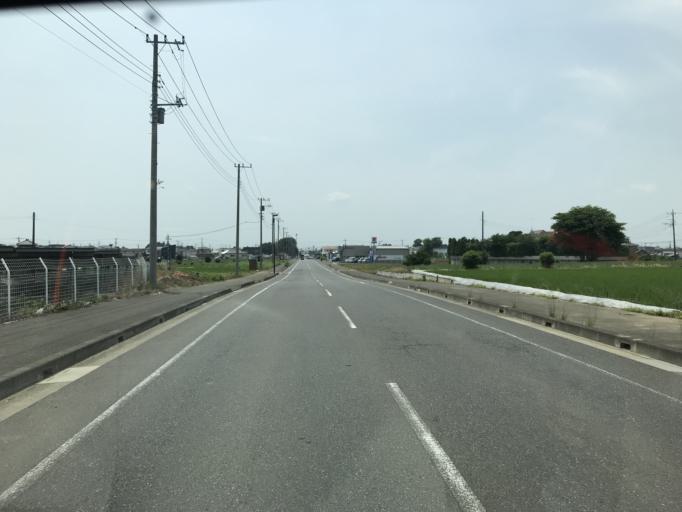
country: JP
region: Ibaraki
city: Sakai
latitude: 36.0396
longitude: 139.8294
